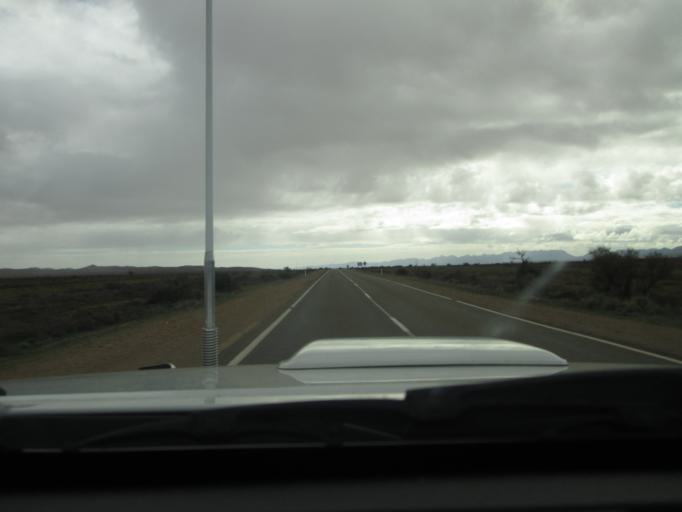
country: AU
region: South Australia
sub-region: Flinders Ranges
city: Quorn
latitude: -31.5427
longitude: 138.4245
